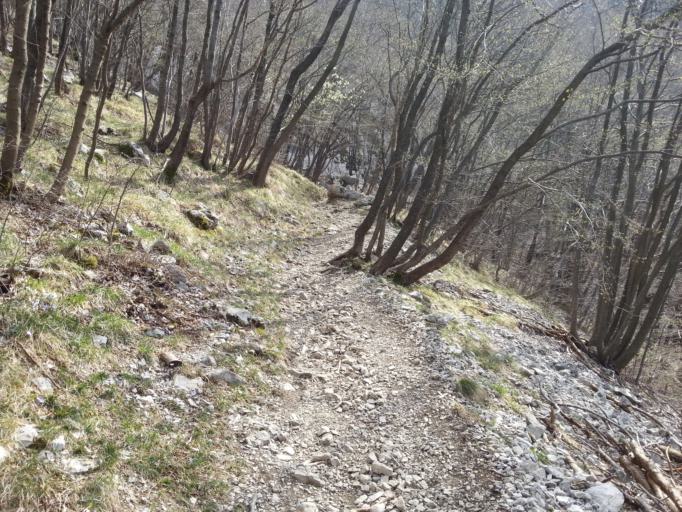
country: IT
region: Lombardy
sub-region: Provincia di Como
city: Valbrona
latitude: 45.8521
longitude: 9.3143
